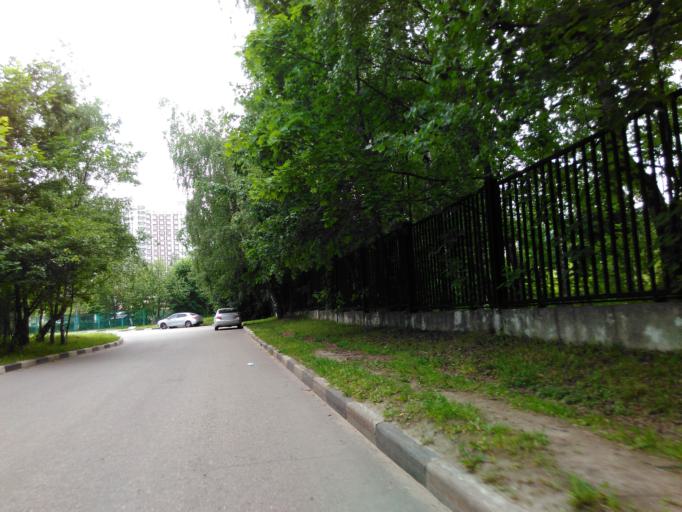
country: RU
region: Moscow
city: Yasenevo
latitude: 55.6163
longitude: 37.5327
